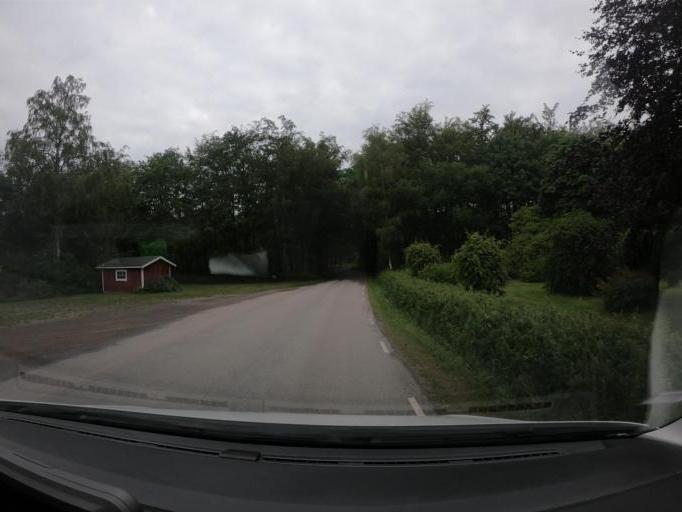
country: SE
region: Skane
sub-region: Angelholms Kommun
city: Munka-Ljungby
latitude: 56.2976
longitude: 13.1146
